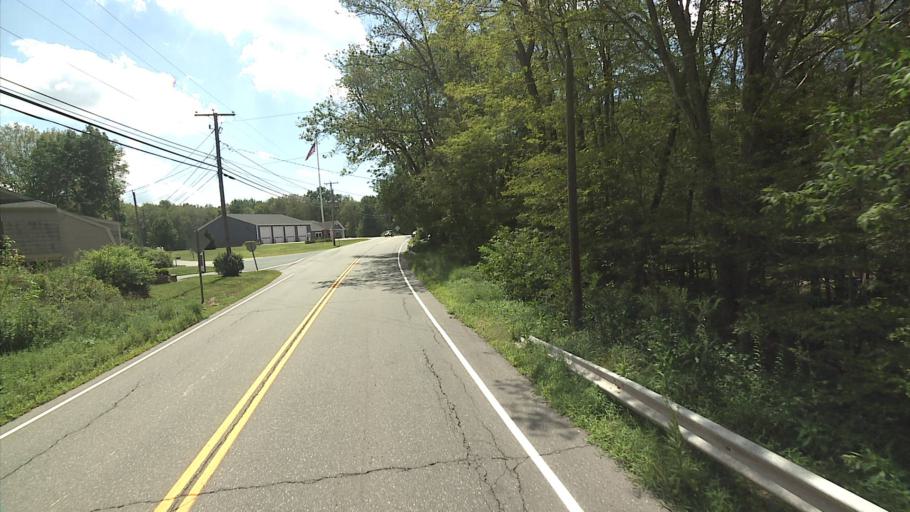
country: US
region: Connecticut
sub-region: Windham County
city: Windham
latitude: 41.7772
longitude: -72.1314
